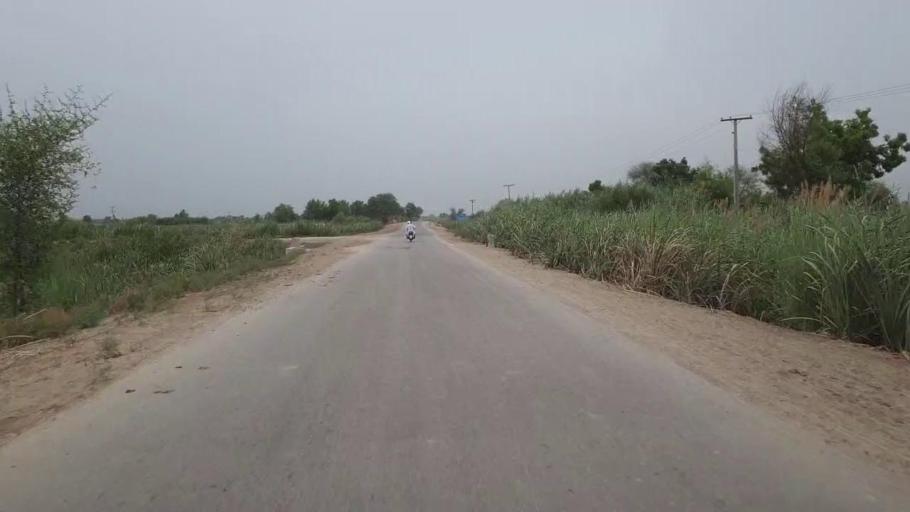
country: PK
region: Sindh
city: Bandhi
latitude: 26.5537
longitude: 68.2109
